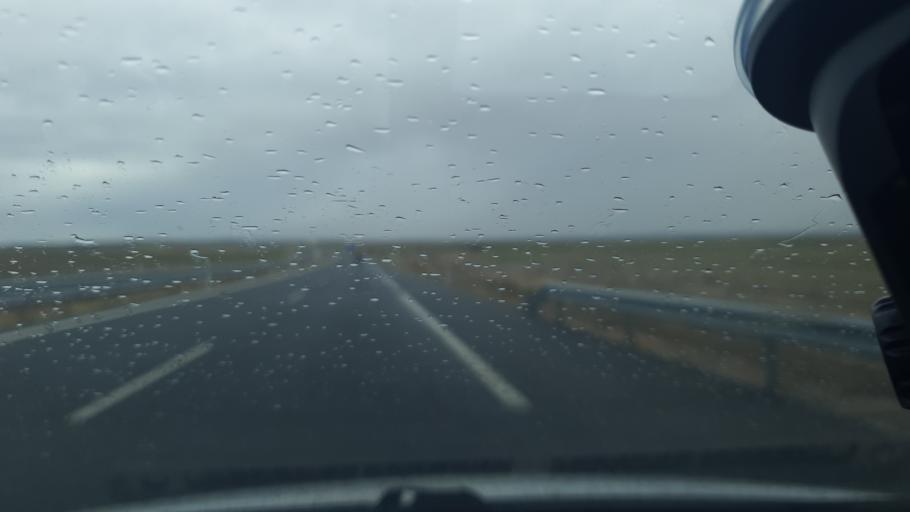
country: ES
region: Castille and Leon
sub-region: Provincia de Segovia
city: Roda de Eresma
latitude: 41.0530
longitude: -4.1968
